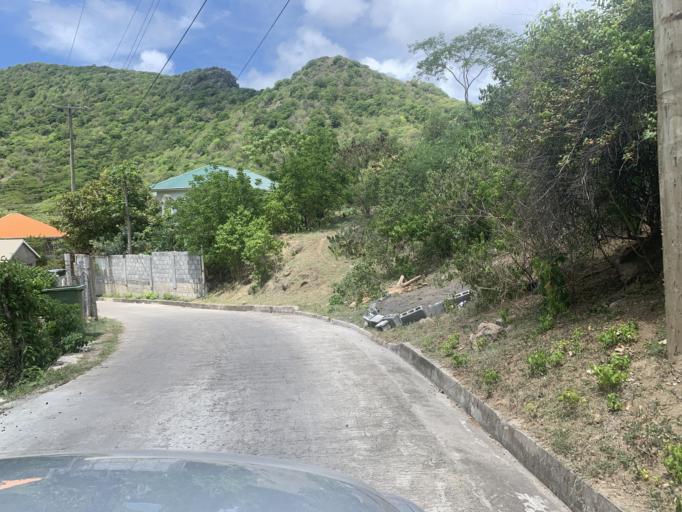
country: GD
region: Carriacou and Petite Martinique
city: Hillsborough
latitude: 12.6035
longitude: -61.4389
